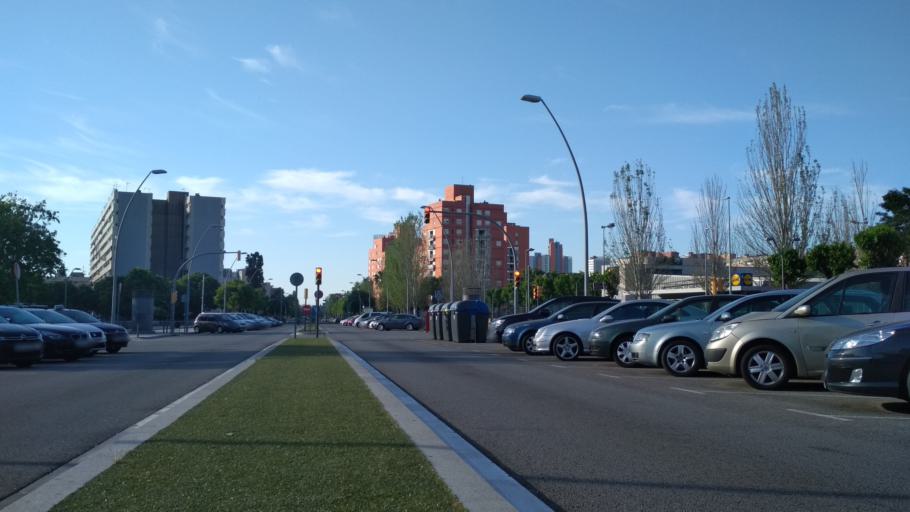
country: ES
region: Catalonia
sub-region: Provincia de Barcelona
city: Sant Adria de Besos
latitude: 41.4206
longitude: 2.2158
